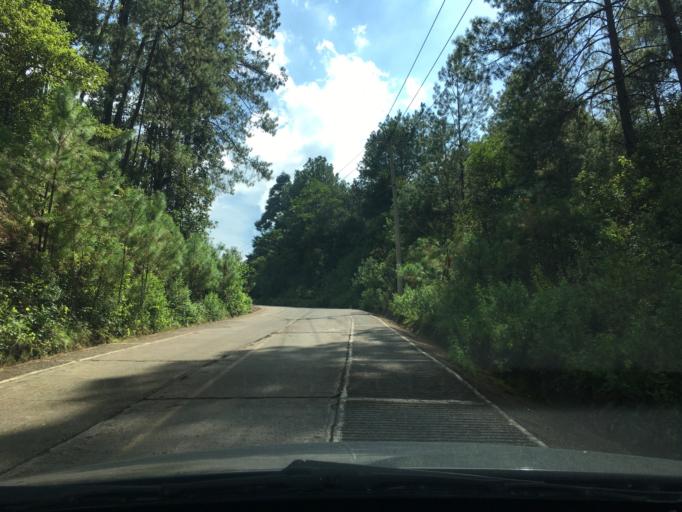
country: MX
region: Michoacan
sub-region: Morelia
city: Morelos
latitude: 19.5642
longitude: -101.1925
